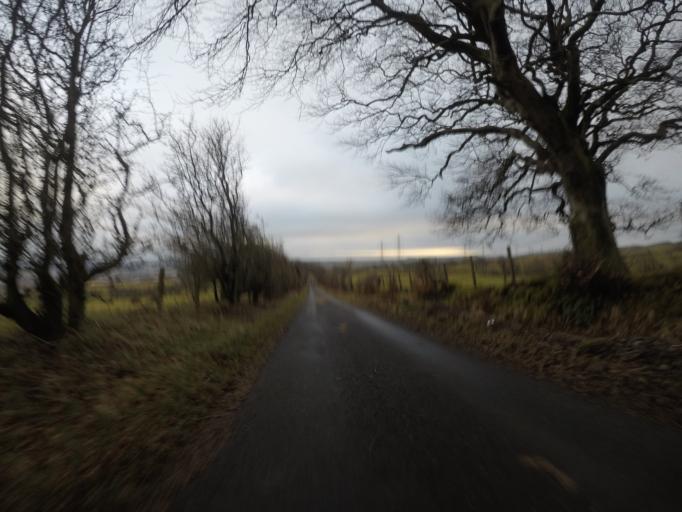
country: GB
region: Scotland
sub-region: North Ayrshire
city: Dalry
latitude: 55.7251
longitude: -4.7635
